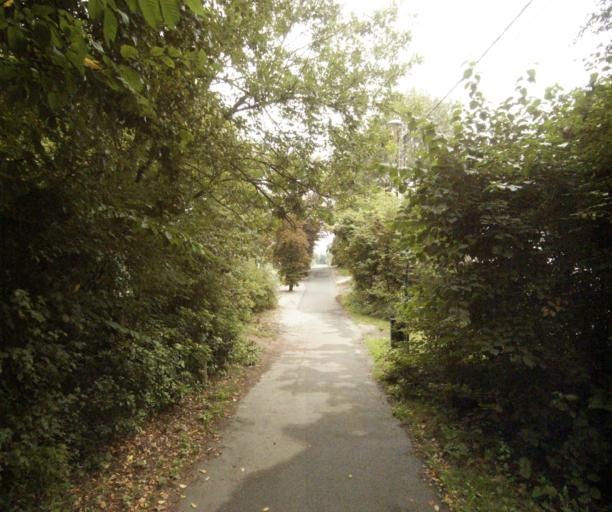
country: FR
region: Nord-Pas-de-Calais
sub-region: Departement du Nord
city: Ronchin
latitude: 50.5976
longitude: 3.0844
